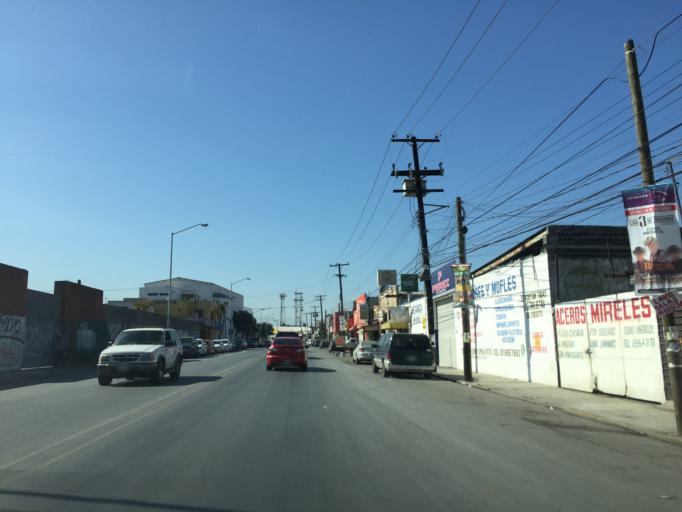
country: MX
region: Nuevo Leon
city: Guadalupe
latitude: 25.6828
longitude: -100.2331
